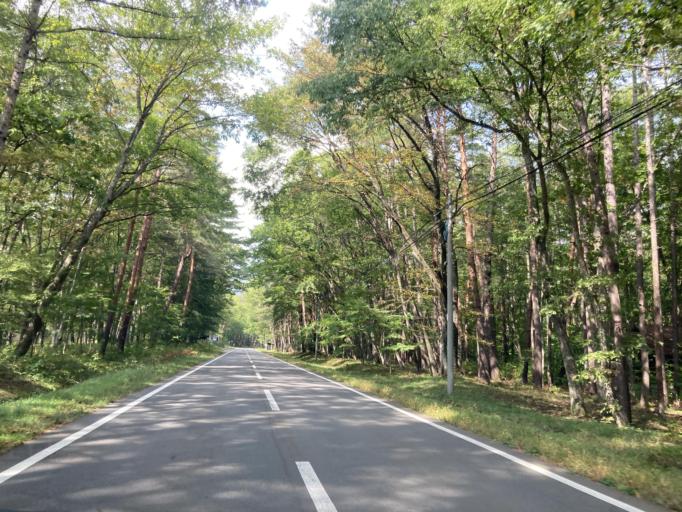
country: JP
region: Nagano
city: Omachi
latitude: 36.5284
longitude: 137.7975
